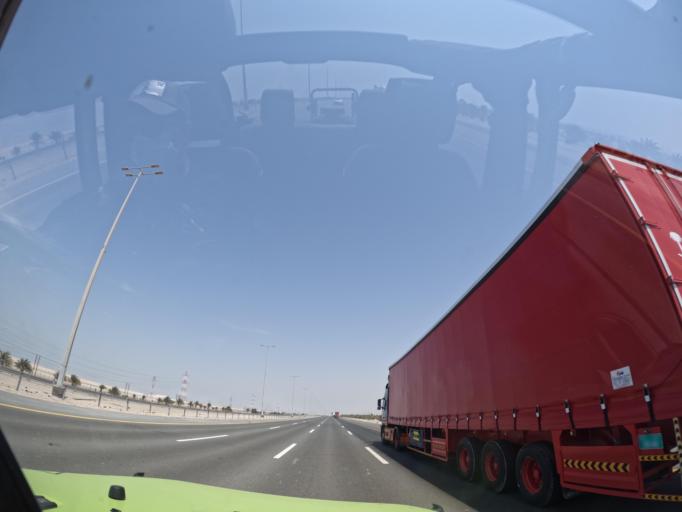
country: AE
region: Abu Dhabi
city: Abu Dhabi
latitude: 24.2002
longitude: 54.3973
